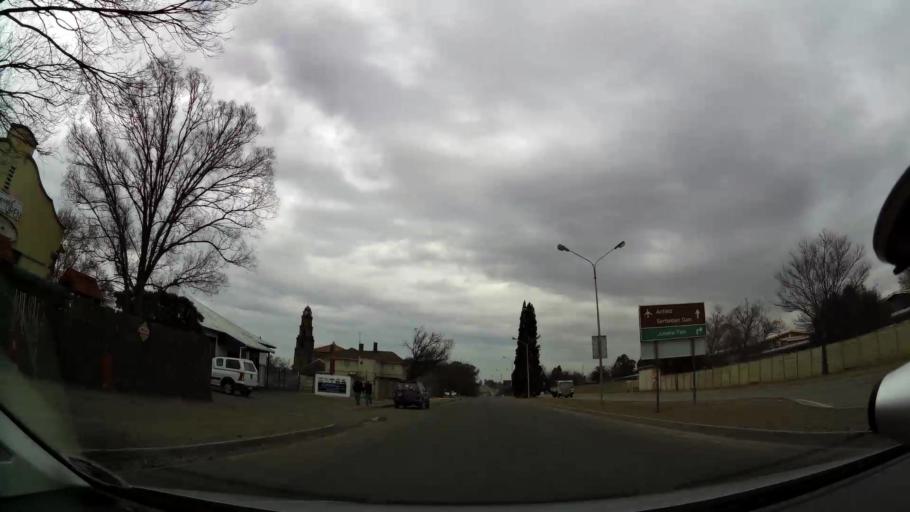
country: ZA
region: Orange Free State
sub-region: Fezile Dabi District Municipality
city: Kroonstad
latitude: -27.6588
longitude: 27.2439
